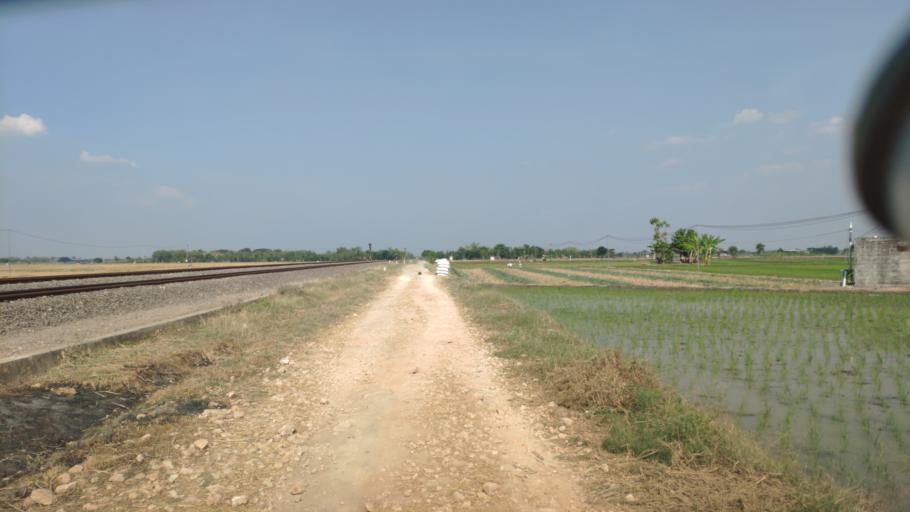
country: ID
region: Central Java
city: Pulo
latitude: -7.1961
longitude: 111.5073
